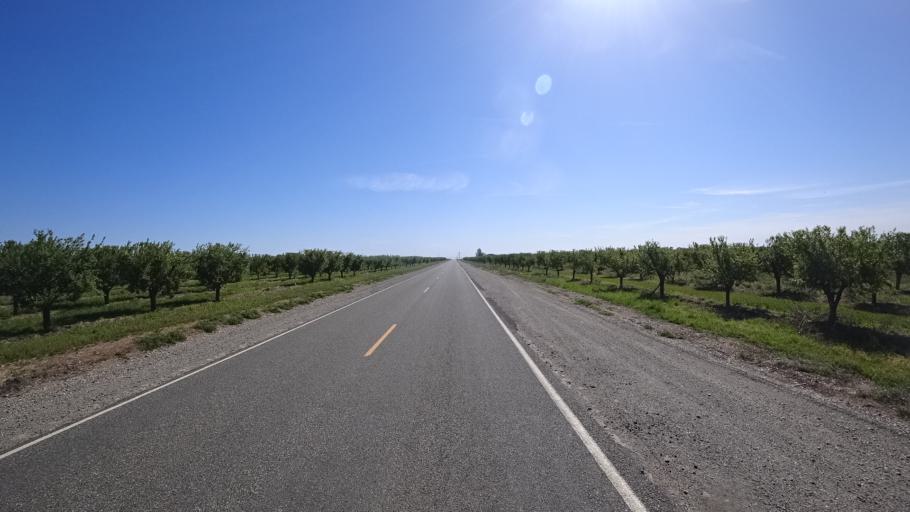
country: US
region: California
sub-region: Glenn County
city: Willows
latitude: 39.6239
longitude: -122.1664
